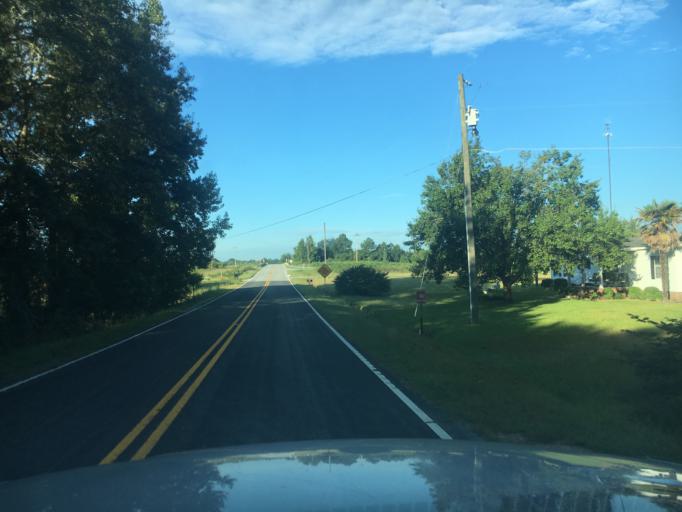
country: US
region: South Carolina
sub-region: Spartanburg County
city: Woodruff
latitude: 34.6180
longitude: -82.0810
